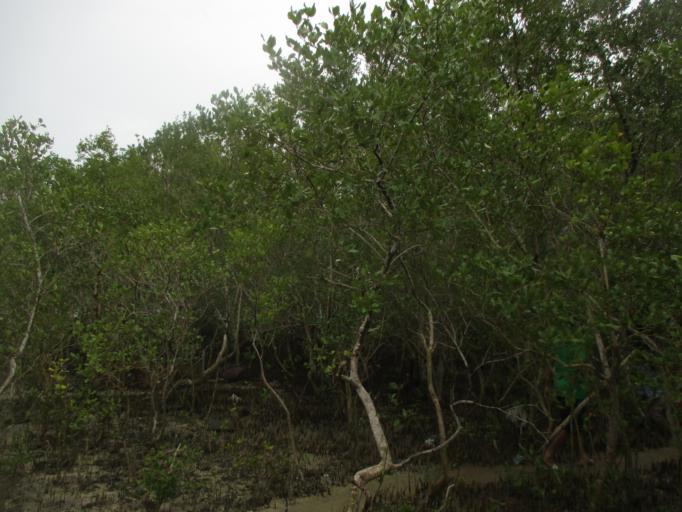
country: PH
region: Calabarzon
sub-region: Province of Batangas
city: Binubusan
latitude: 13.9962
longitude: 120.6238
